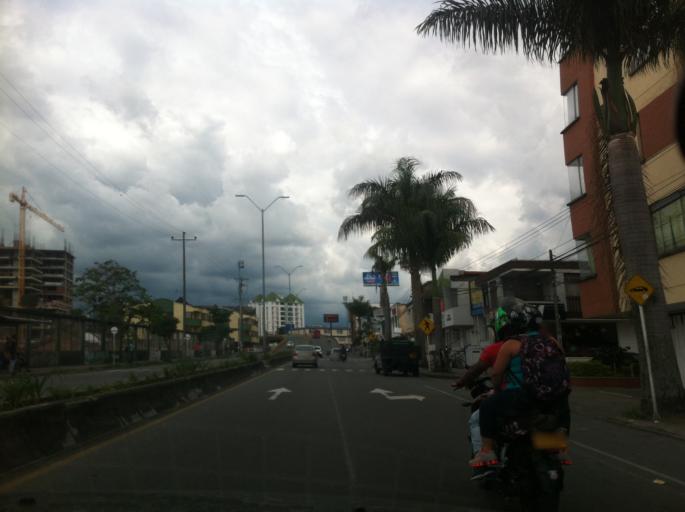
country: CO
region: Quindio
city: Armenia
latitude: 4.5404
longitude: -75.6650
